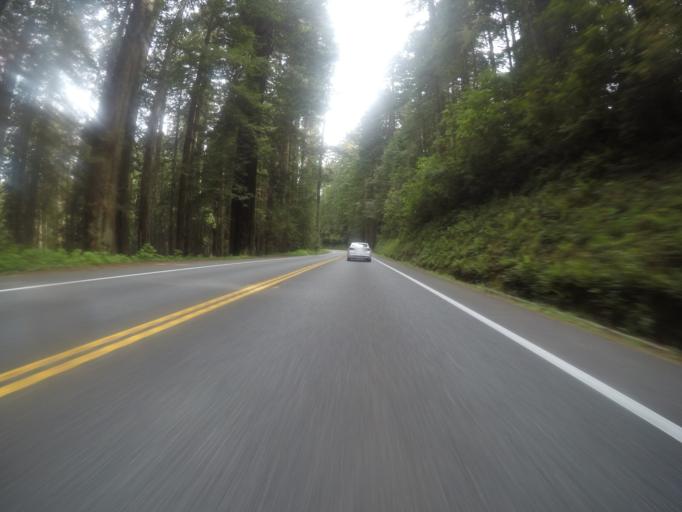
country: US
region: California
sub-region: Del Norte County
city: Bertsch-Oceanview
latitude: 41.6565
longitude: -124.1156
